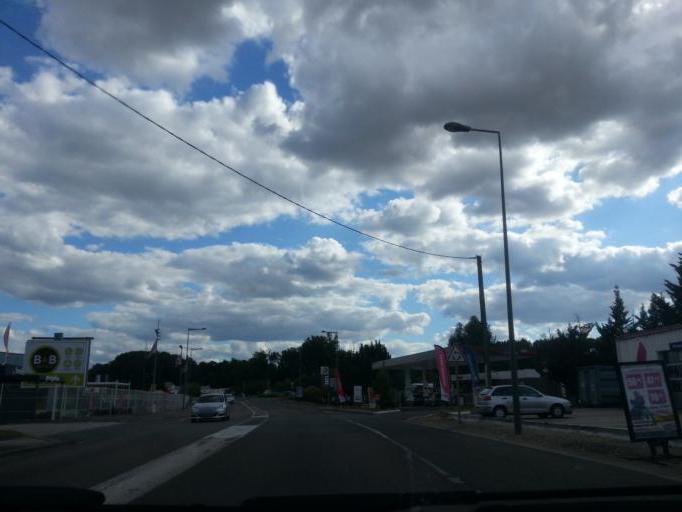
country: FR
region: Bourgogne
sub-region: Departement de Saone-et-Loire
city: Saint-Remy
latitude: 46.7665
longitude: 4.8428
